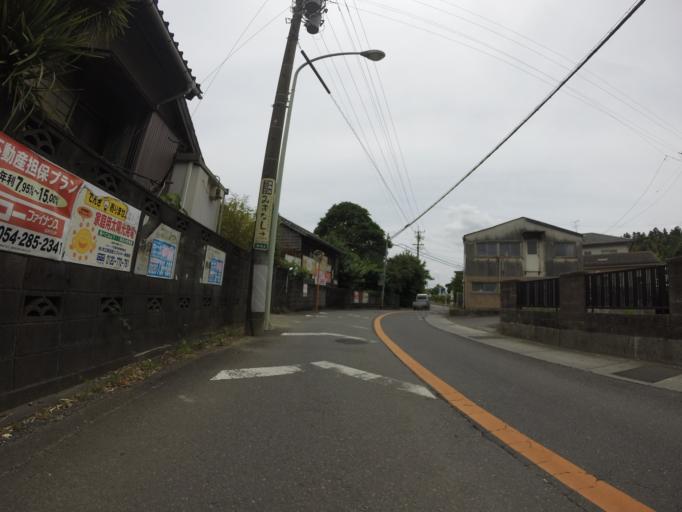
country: JP
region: Shizuoka
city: Shizuoka-shi
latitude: 35.0206
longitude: 138.4182
